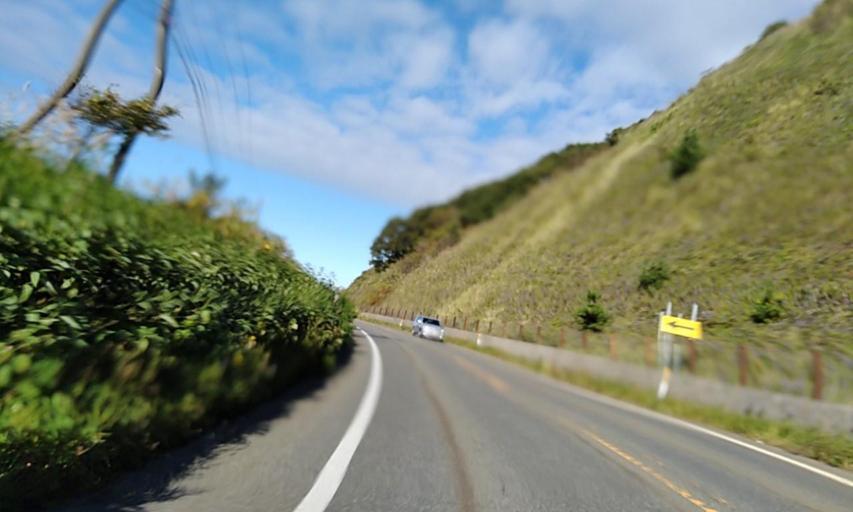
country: JP
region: Hokkaido
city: Shizunai-furukawacho
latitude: 42.3109
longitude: 142.4247
